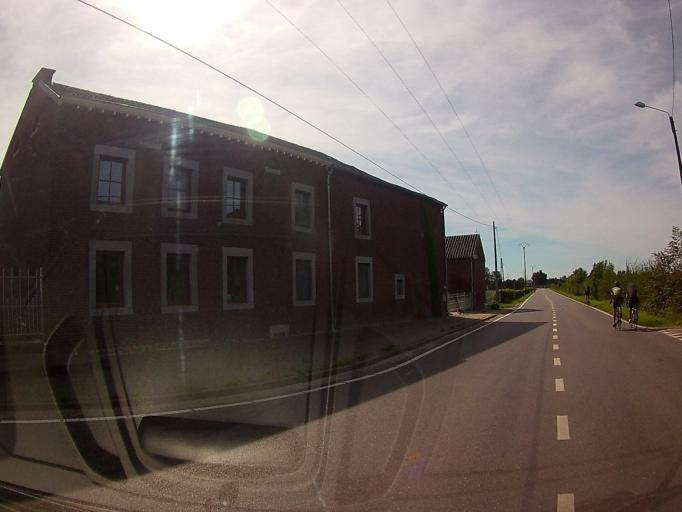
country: BE
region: Wallonia
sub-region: Province de Liege
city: Aubel
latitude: 50.7231
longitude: 5.8664
